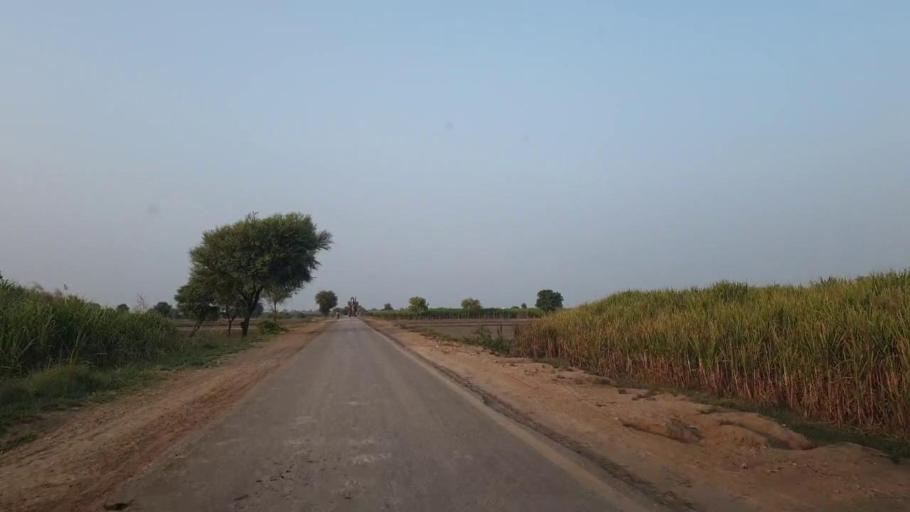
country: PK
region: Sindh
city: Tando Ghulam Ali
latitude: 25.1303
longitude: 68.9587
